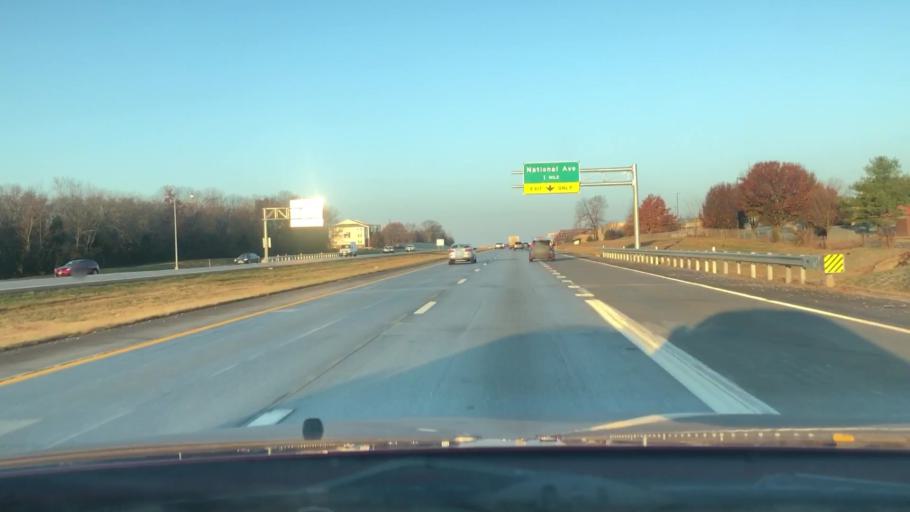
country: US
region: Missouri
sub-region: Greene County
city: Springfield
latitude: 37.1403
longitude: -93.2579
